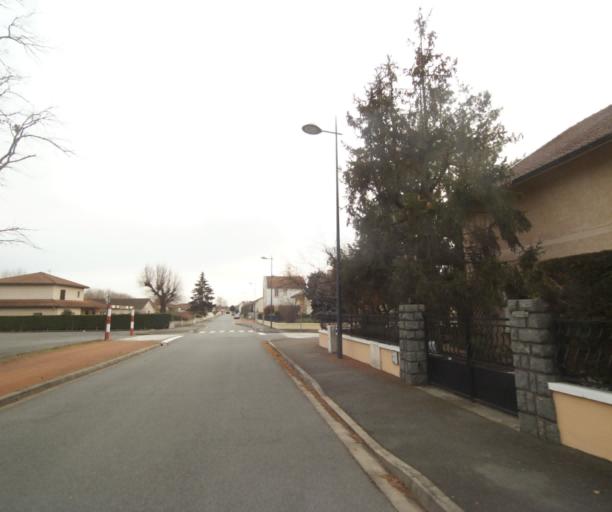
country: FR
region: Rhone-Alpes
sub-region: Departement de la Loire
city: Mably
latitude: 46.0636
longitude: 4.0741
